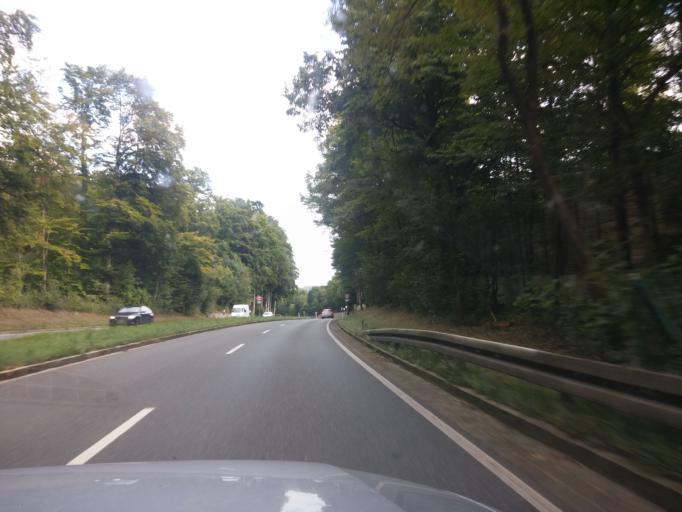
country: DE
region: Bavaria
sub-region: Upper Bavaria
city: Kirchseeon
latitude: 48.0734
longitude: 11.8969
